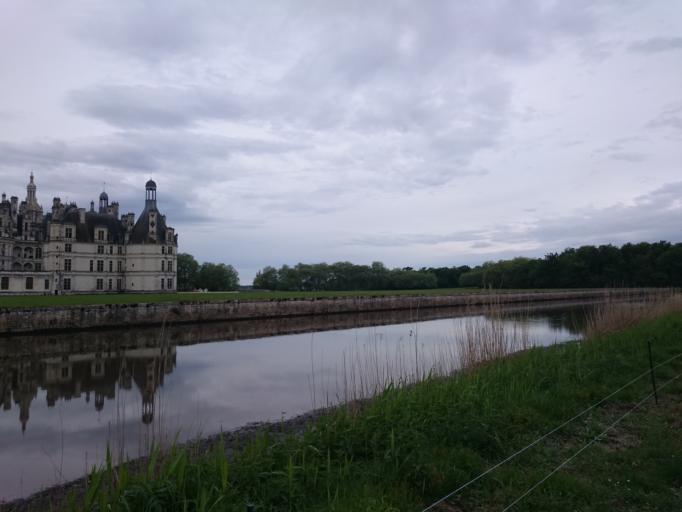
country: FR
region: Centre
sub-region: Departement du Loir-et-Cher
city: Saint-Dye-sur-Loire
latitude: 47.6172
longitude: 1.5202
